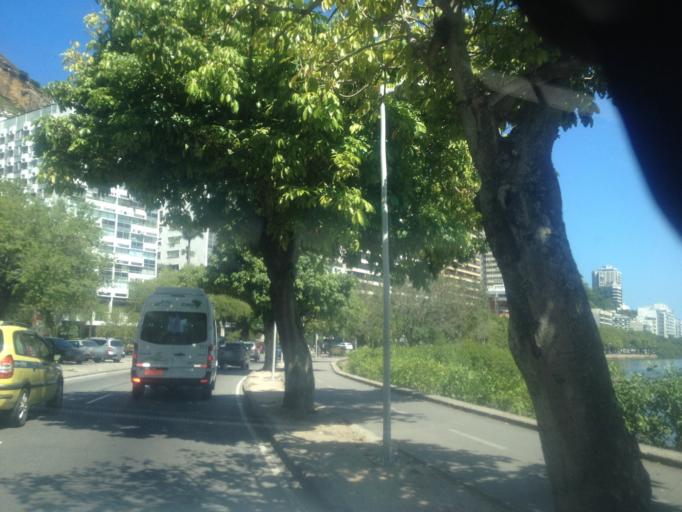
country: BR
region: Rio de Janeiro
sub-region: Rio De Janeiro
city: Rio de Janeiro
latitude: -22.9663
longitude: -43.2035
